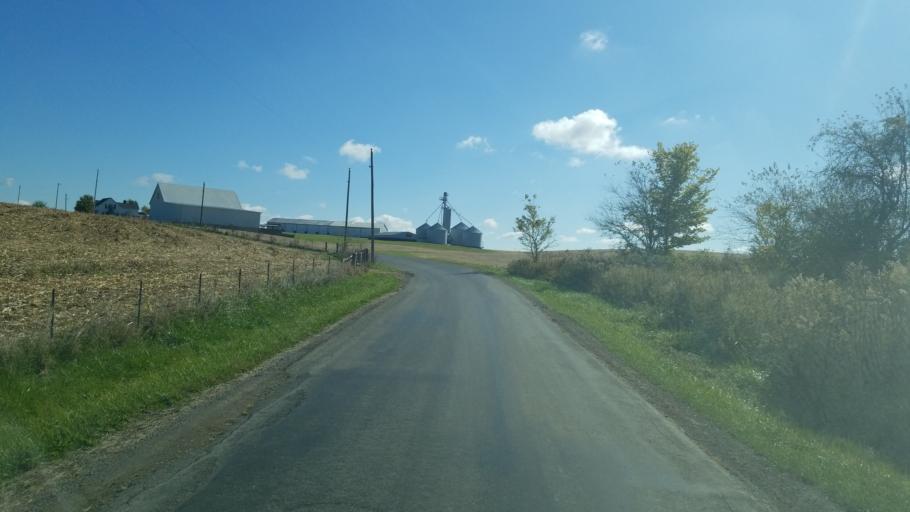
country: US
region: Ohio
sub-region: Highland County
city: Leesburg
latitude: 39.2767
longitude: -83.5633
